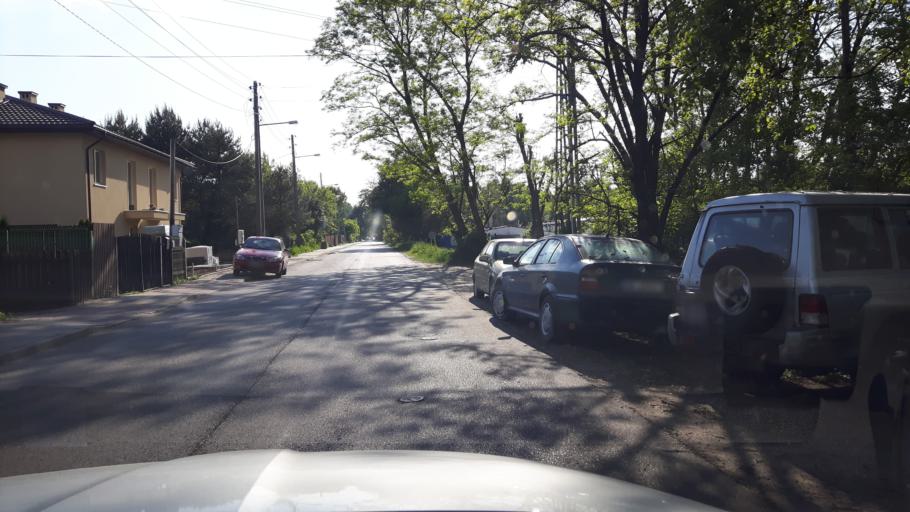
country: PL
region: Masovian Voivodeship
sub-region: Powiat wolominski
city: Zabki
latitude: 52.2579
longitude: 21.1231
